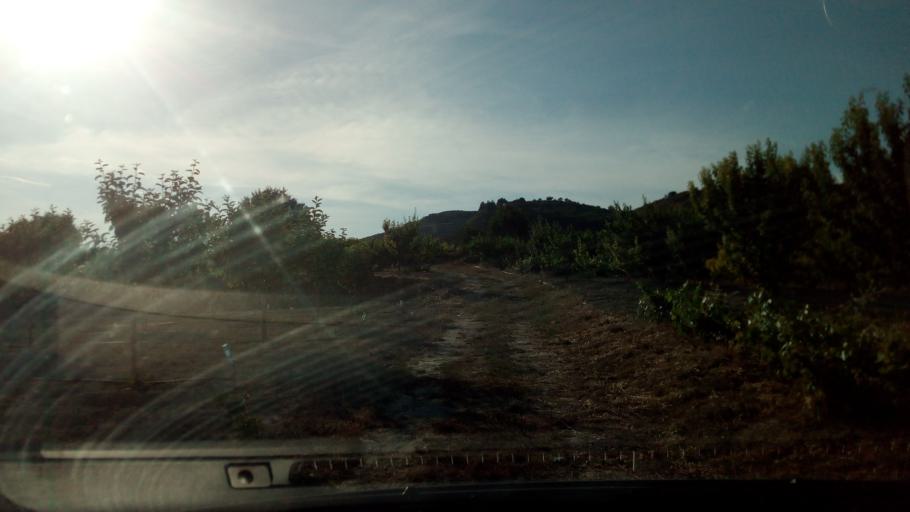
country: CY
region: Pafos
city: Tala
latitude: 34.8731
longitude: 32.4774
